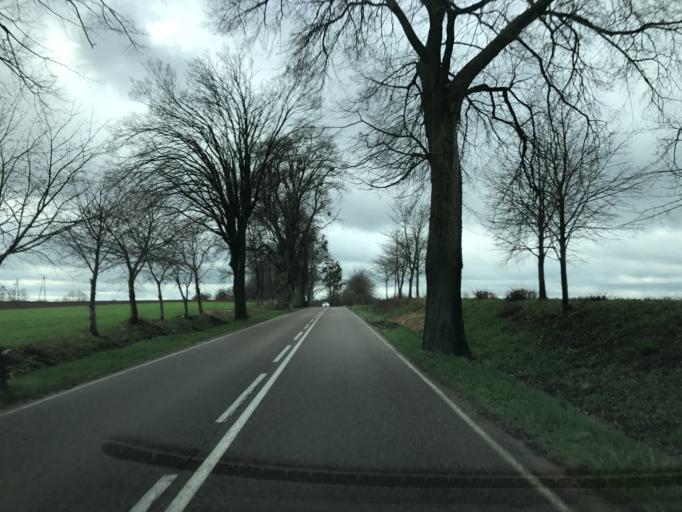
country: PL
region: Warmian-Masurian Voivodeship
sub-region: Powiat olsztynski
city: Olsztynek
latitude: 53.5318
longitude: 20.2570
